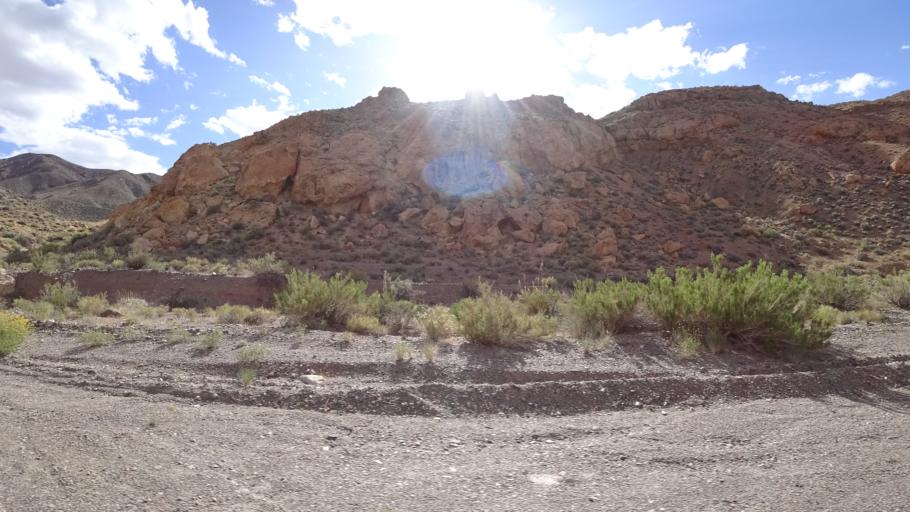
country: US
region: Nevada
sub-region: Nye County
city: Beatty
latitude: 36.4263
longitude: -117.1930
